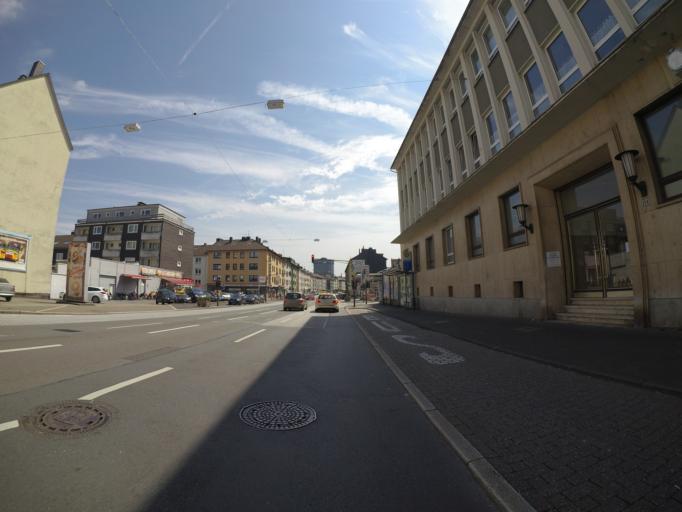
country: DE
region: North Rhine-Westphalia
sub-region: Regierungsbezirk Dusseldorf
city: Wuppertal
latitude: 51.2711
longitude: 7.2177
